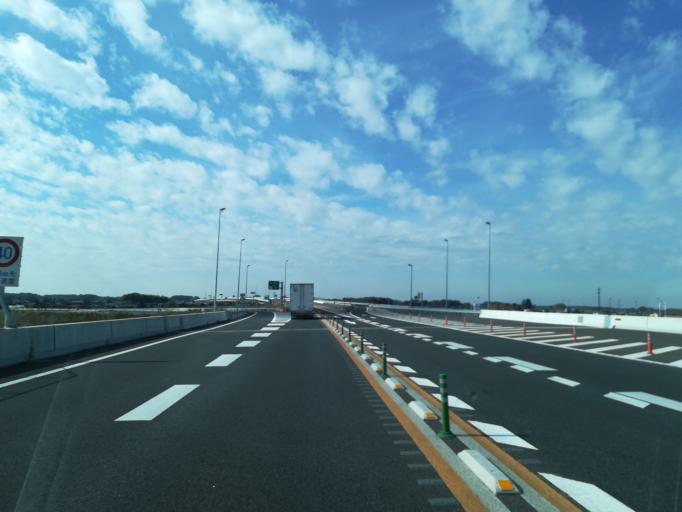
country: JP
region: Ibaraki
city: Ishige
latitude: 36.0786
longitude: 139.9861
